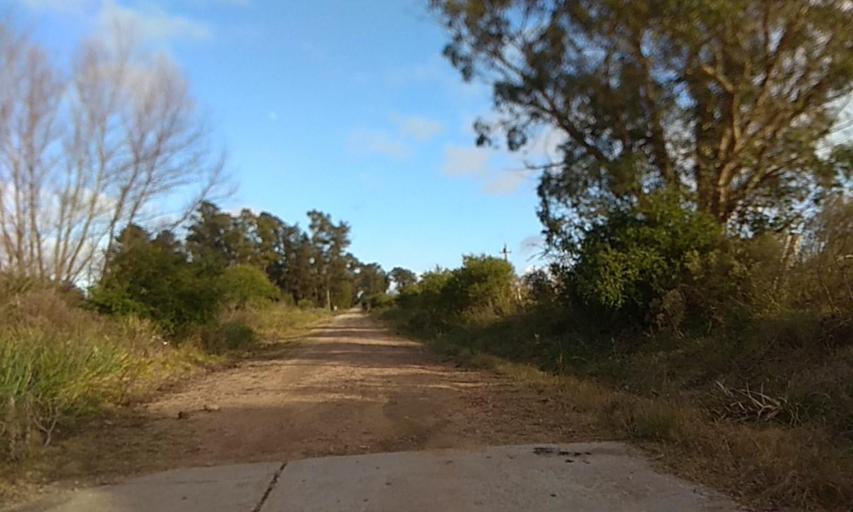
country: UY
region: Florida
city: Florida
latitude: -34.0433
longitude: -56.1982
